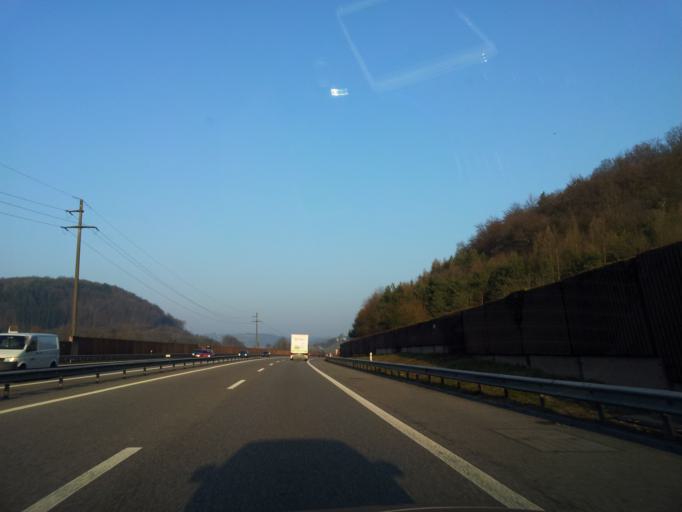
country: CH
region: Aargau
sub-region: Bezirk Laufenburg
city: Sulz
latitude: 47.4994
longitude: 8.0703
